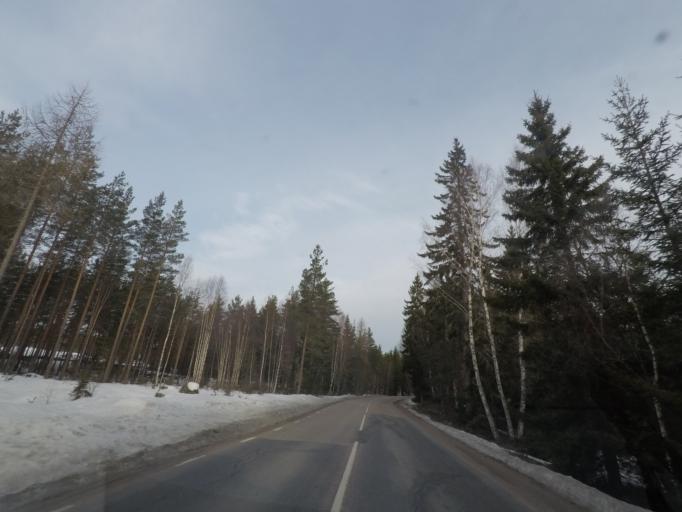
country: SE
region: Vaestmanland
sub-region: Surahammars Kommun
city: Surahammar
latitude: 59.7615
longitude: 16.2960
